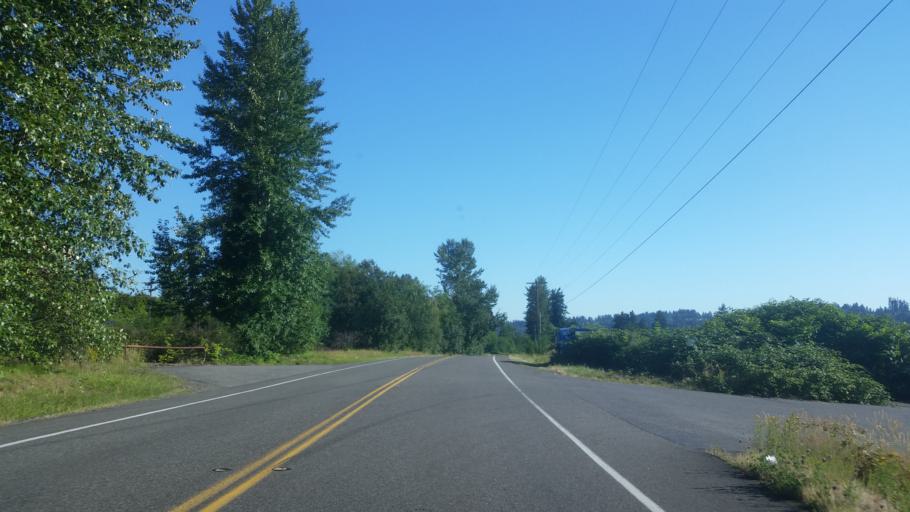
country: US
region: Washington
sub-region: King County
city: Woodinville
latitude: 47.7633
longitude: -122.1546
